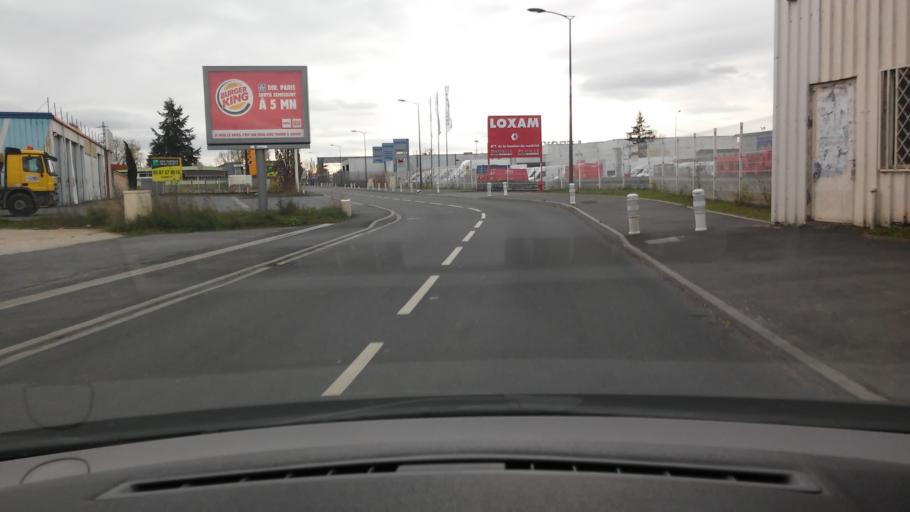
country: FR
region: Lorraine
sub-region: Departement de la Moselle
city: Talange
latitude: 49.2222
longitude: 6.1787
